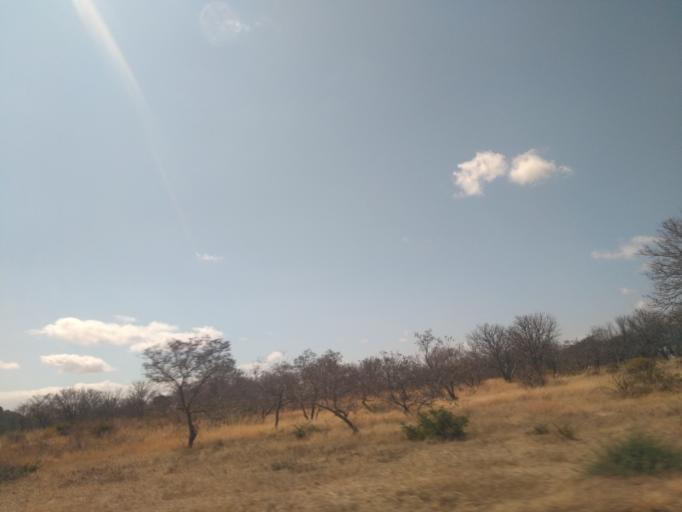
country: TZ
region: Dodoma
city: Dodoma
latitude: -6.1573
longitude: 35.7573
